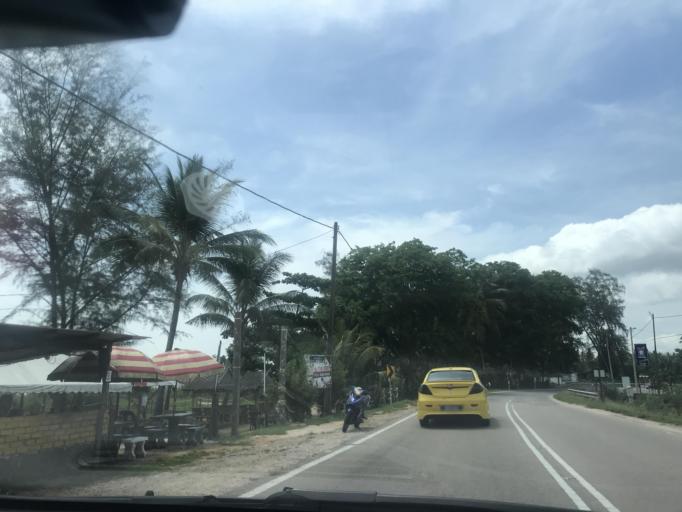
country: MY
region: Kelantan
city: Tumpat
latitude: 6.2073
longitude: 102.1429
